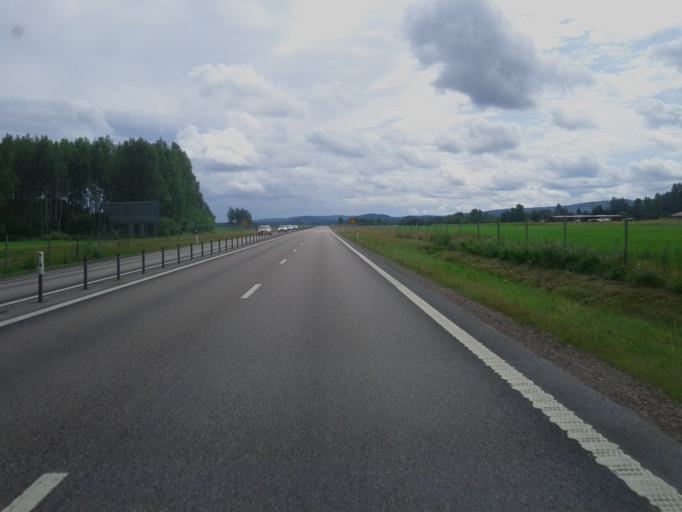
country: SE
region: Dalarna
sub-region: Borlange Kommun
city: Ornas
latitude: 60.4339
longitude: 15.5160
